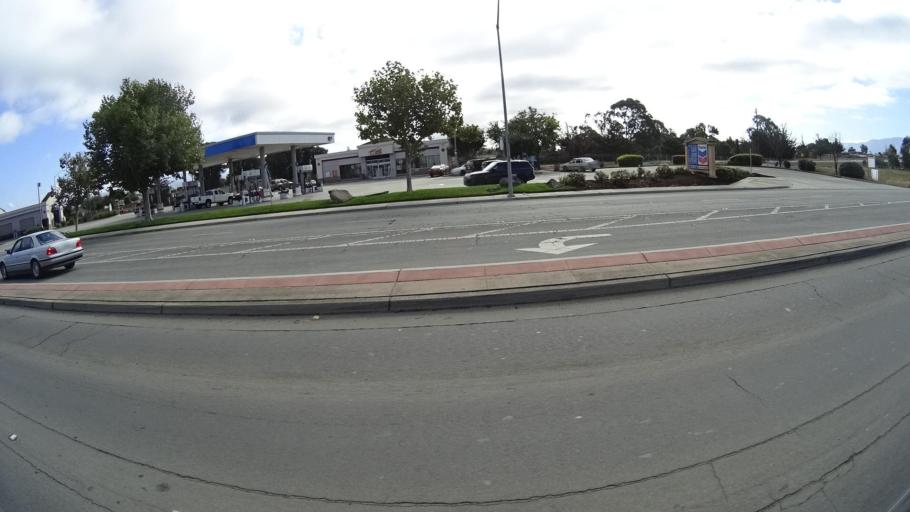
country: US
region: California
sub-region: Monterey County
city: Boronda
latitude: 36.7008
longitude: -121.6671
